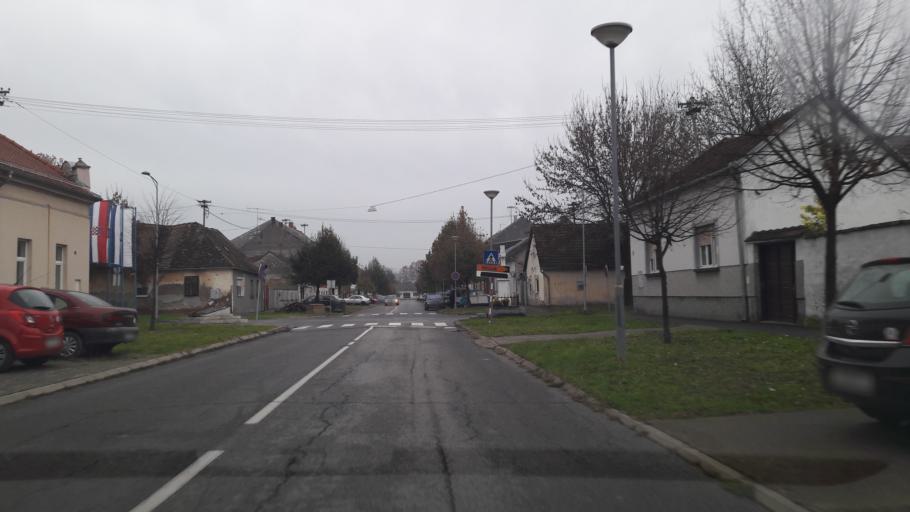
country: HR
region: Osjecko-Baranjska
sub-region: Grad Osijek
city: Osijek
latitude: 45.5581
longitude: 18.6663
